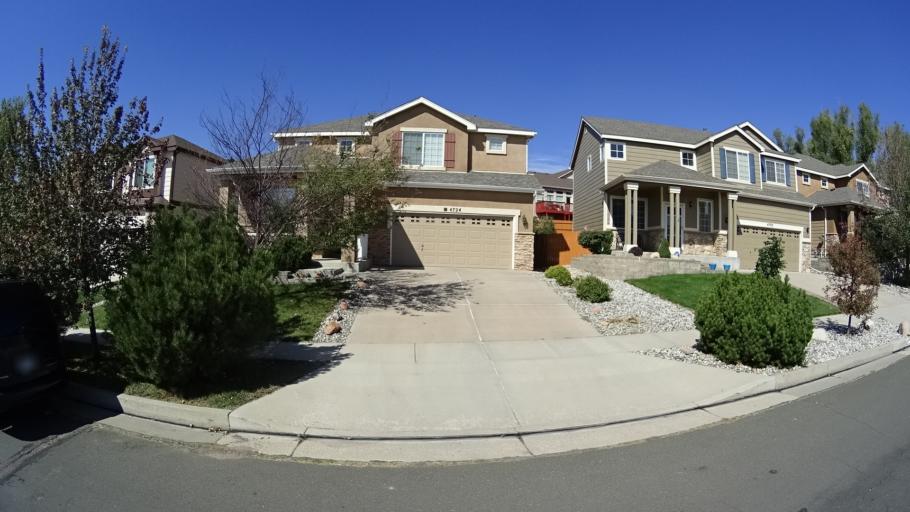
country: US
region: Colorado
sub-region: El Paso County
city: Cimarron Hills
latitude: 38.8996
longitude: -104.6909
